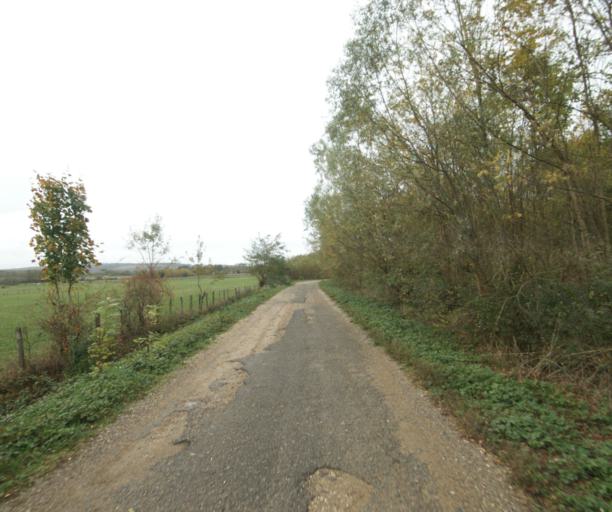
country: FR
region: Rhone-Alpes
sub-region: Departement de l'Ain
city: Pont-de-Vaux
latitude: 46.4604
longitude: 4.8969
